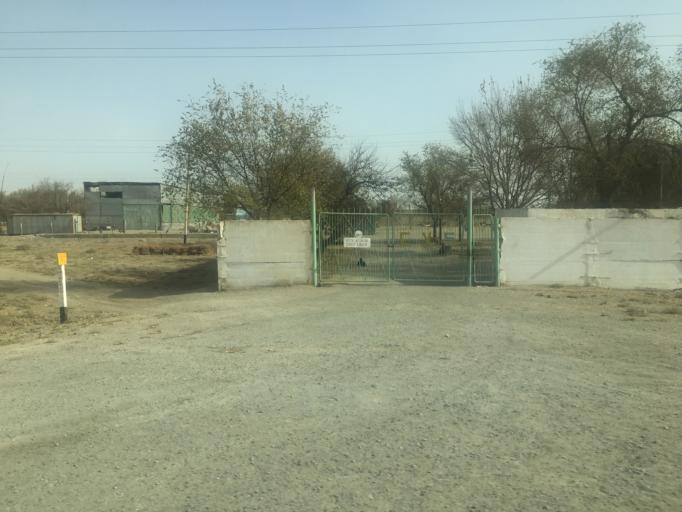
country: TM
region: Lebap
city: Gazojak
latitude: 41.1683
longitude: 61.3981
